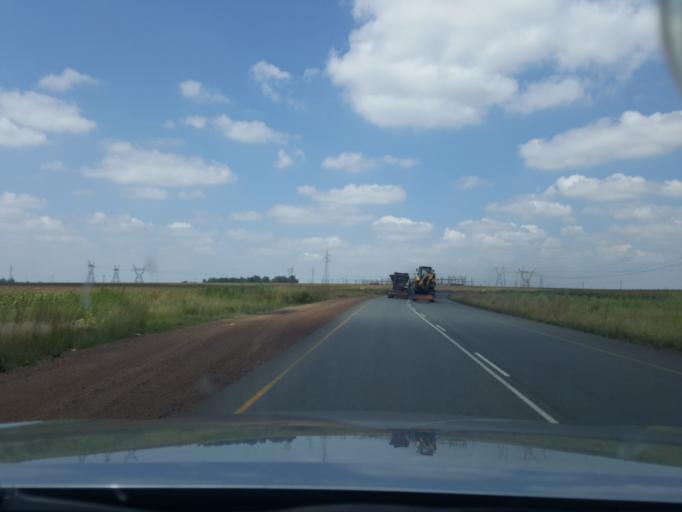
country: ZA
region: Mpumalanga
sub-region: Nkangala District Municipality
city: Witbank
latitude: -26.0141
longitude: 29.4120
